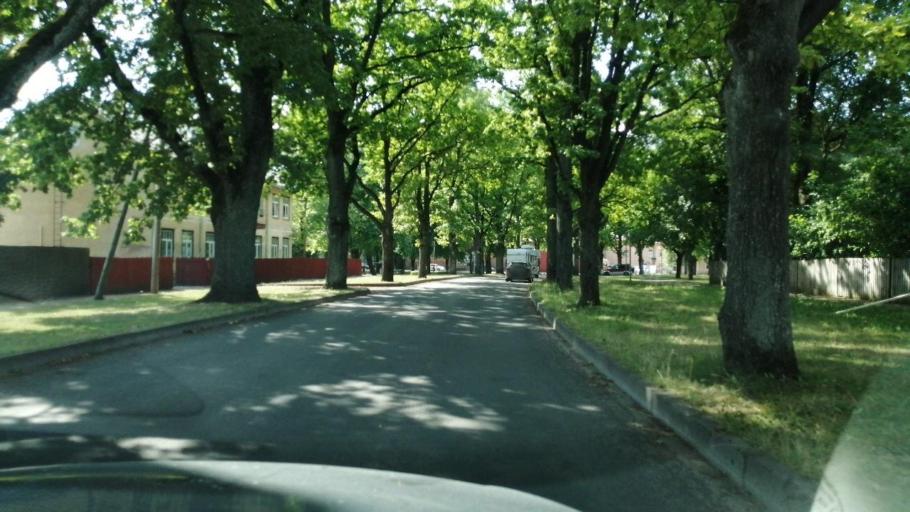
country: EE
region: Viljandimaa
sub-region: Viljandi linn
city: Viljandi
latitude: 58.3692
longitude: 25.6025
